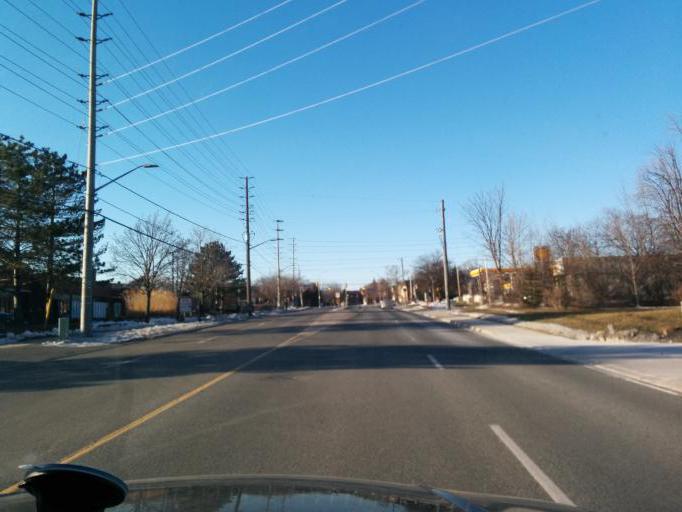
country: CA
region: Ontario
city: Mississauga
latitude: 43.5697
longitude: -79.6599
